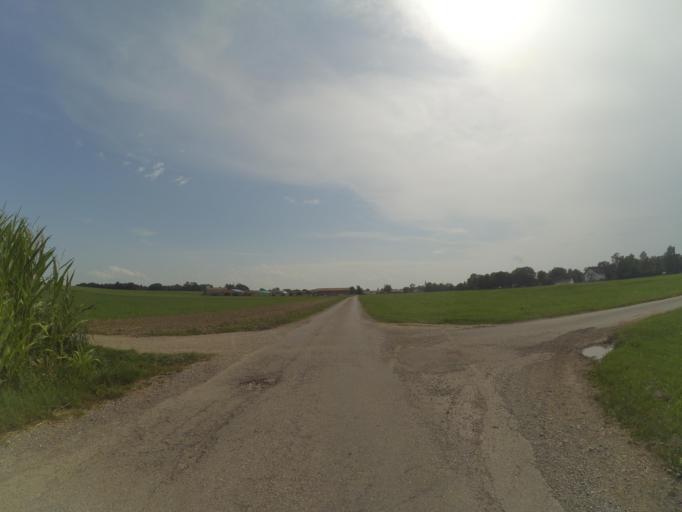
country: DE
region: Bavaria
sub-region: Swabia
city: Jengen
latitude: 48.0091
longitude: 10.7270
